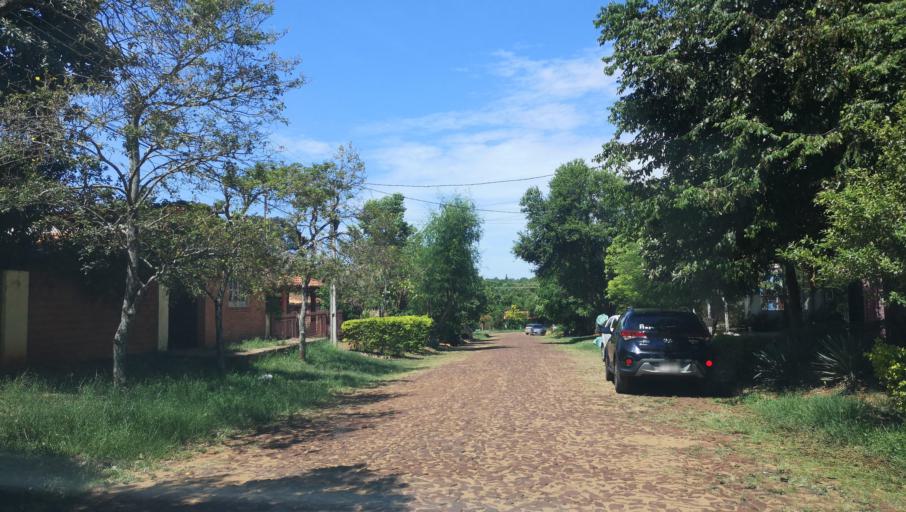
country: PY
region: Misiones
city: Santa Maria
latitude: -26.8815
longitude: -57.0300
